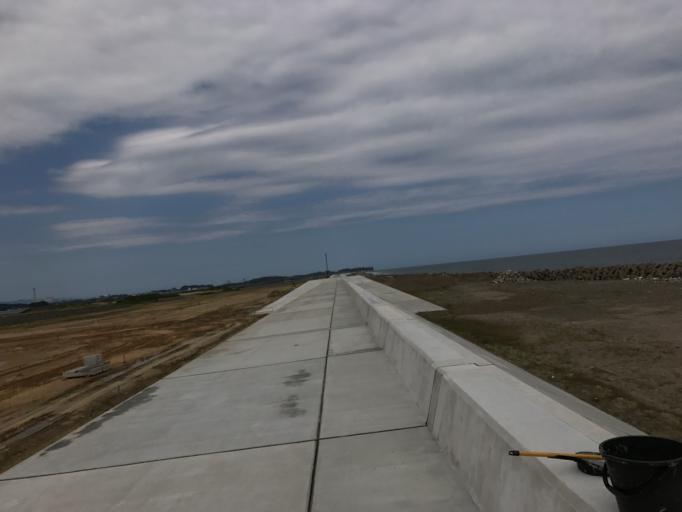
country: JP
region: Miyagi
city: Marumori
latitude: 37.7879
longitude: 140.9866
